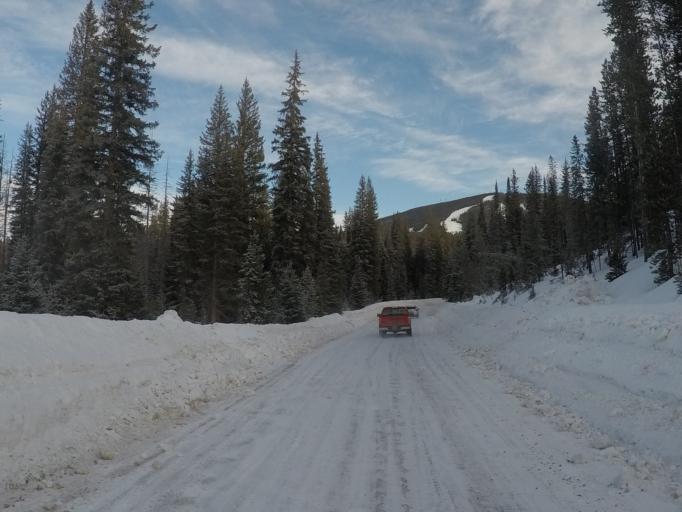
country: US
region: Montana
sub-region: Granite County
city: Philipsburg
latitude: 46.2393
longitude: -113.2432
